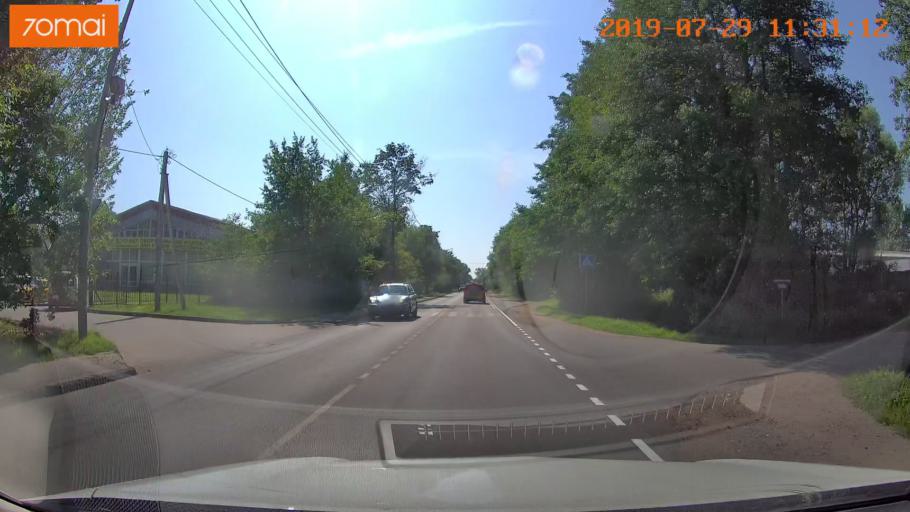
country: RU
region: Kaliningrad
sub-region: Gorod Kaliningrad
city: Kaliningrad
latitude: 54.6766
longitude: 20.5401
